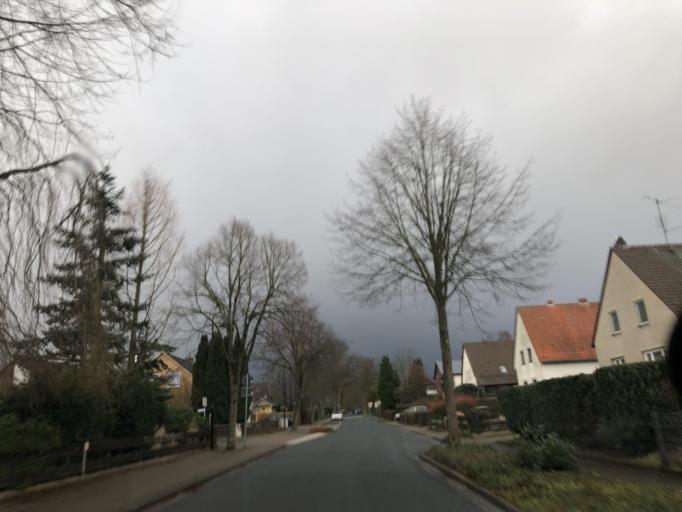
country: DE
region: Lower Saxony
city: Bad Fallingbostel
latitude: 52.8810
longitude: 9.7079
